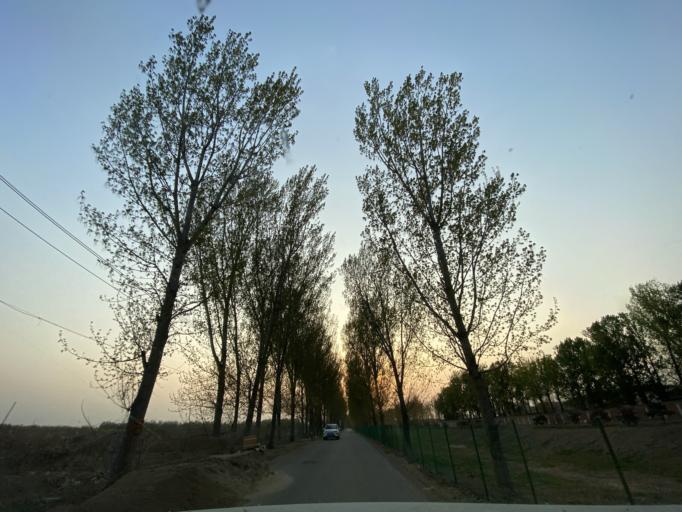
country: CN
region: Beijing
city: Weishanzhuang
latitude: 39.6064
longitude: 116.4182
